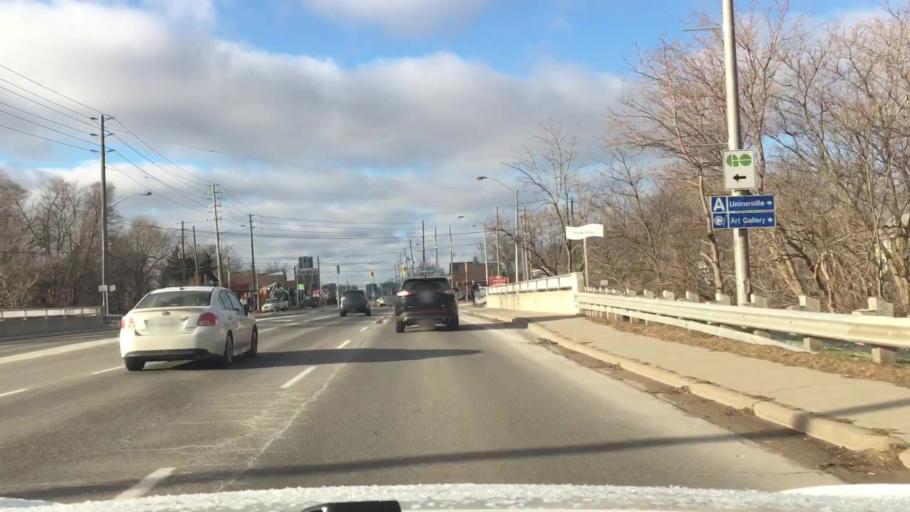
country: CA
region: Ontario
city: Markham
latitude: 43.8618
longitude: -79.3082
